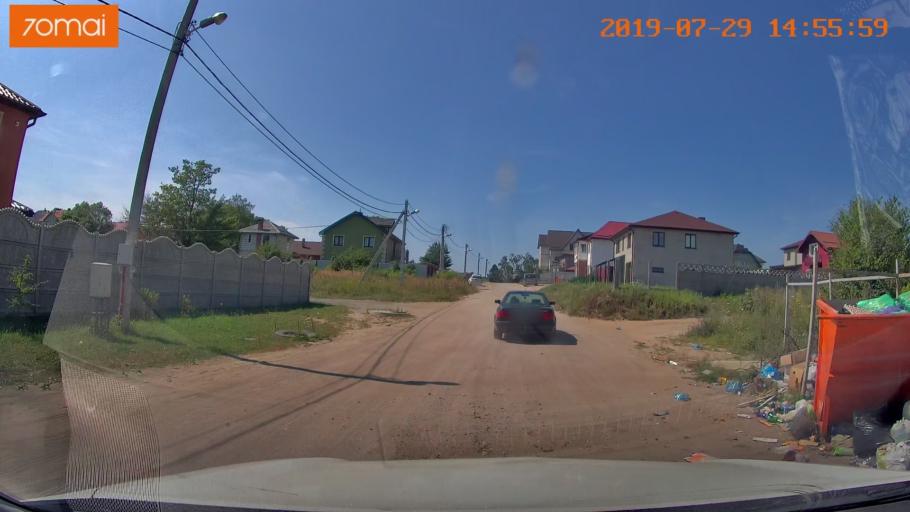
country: RU
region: Kaliningrad
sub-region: Gorod Kaliningrad
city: Baltiysk
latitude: 54.6795
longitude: 19.9235
